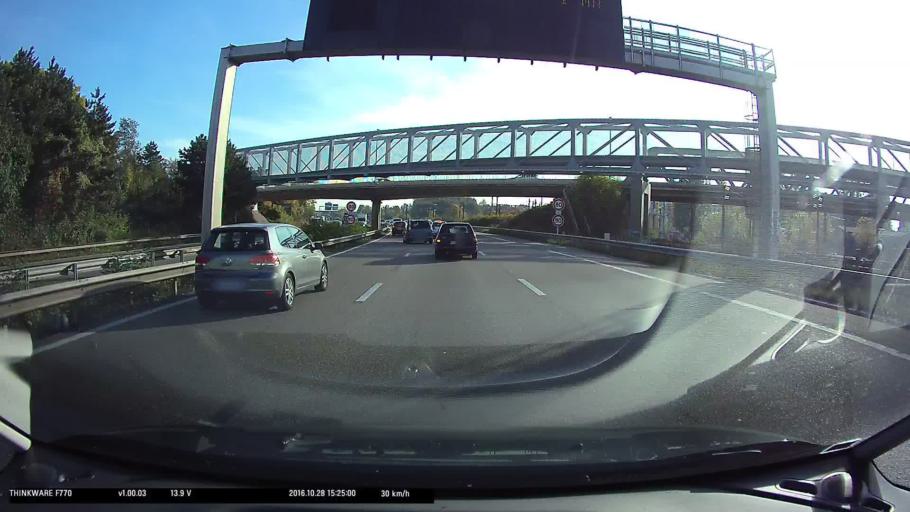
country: FR
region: Alsace
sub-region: Departement du Bas-Rhin
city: Schiltigheim
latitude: 48.6071
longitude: 7.7272
